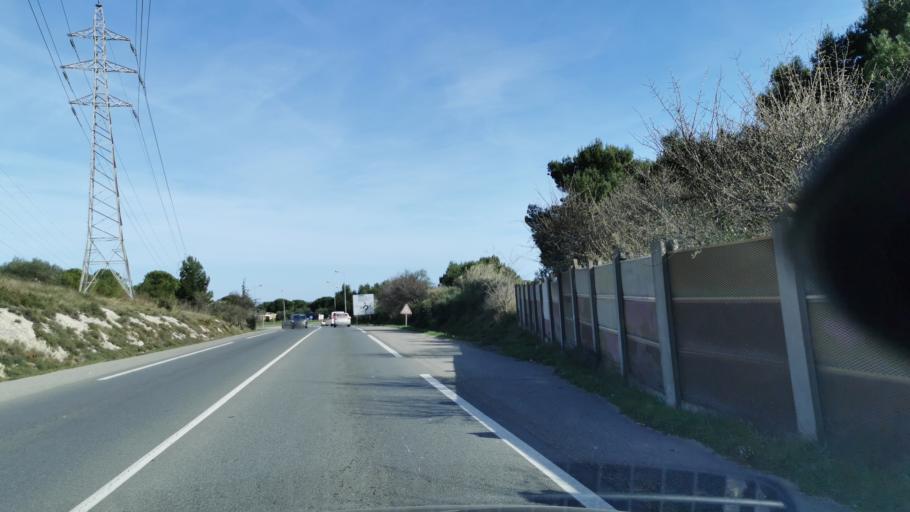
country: FR
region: Languedoc-Roussillon
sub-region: Departement de l'Aude
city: Narbonne
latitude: 43.1849
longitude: 2.9705
